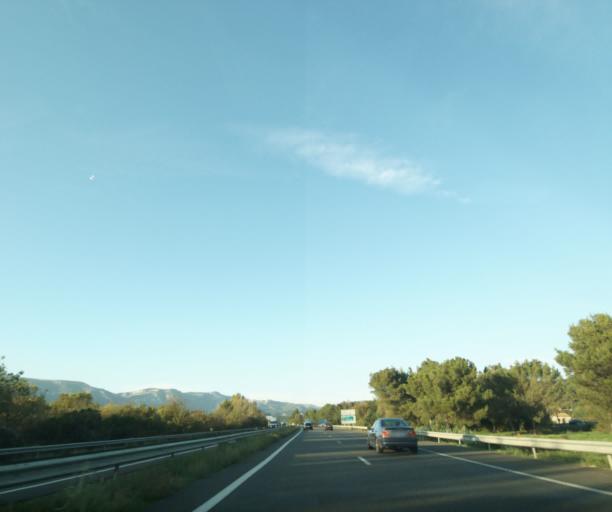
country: FR
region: Provence-Alpes-Cote d'Azur
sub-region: Departement des Bouches-du-Rhone
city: Aubagne
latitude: 43.3077
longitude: 5.5921
